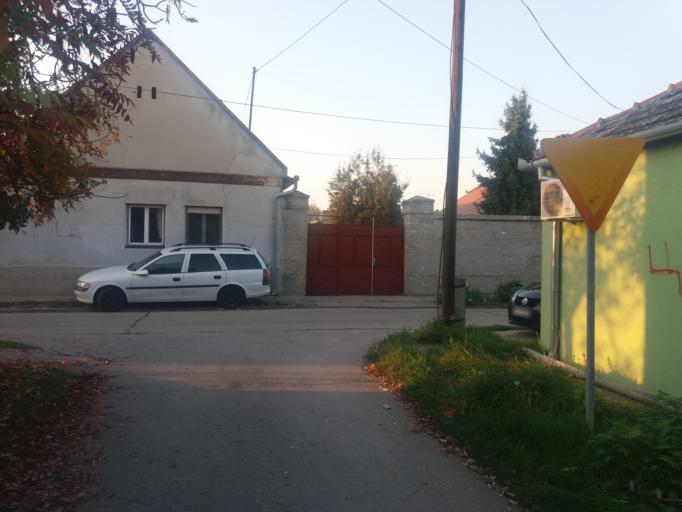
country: RS
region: Autonomna Pokrajina Vojvodina
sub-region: Severnobacki Okrug
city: Subotica
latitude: 46.0984
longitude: 19.6528
